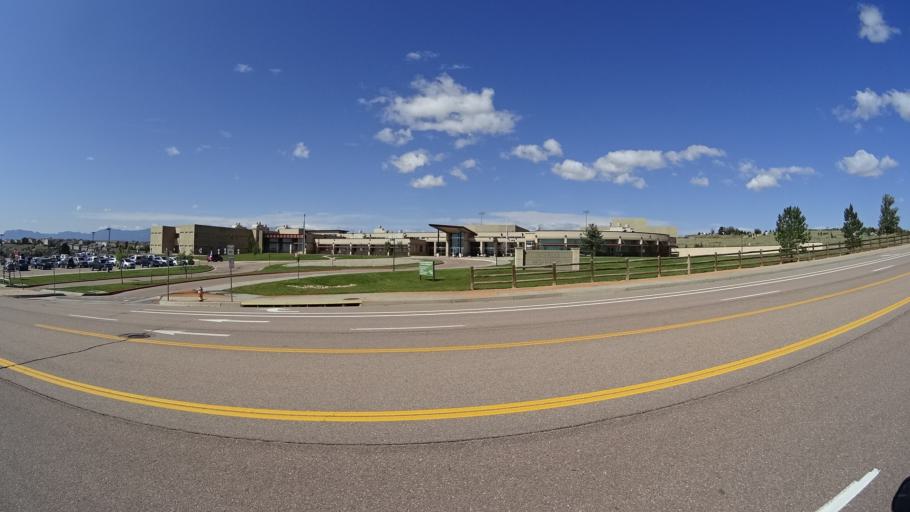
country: US
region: Colorado
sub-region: El Paso County
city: Cimarron Hills
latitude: 38.9315
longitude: -104.7010
